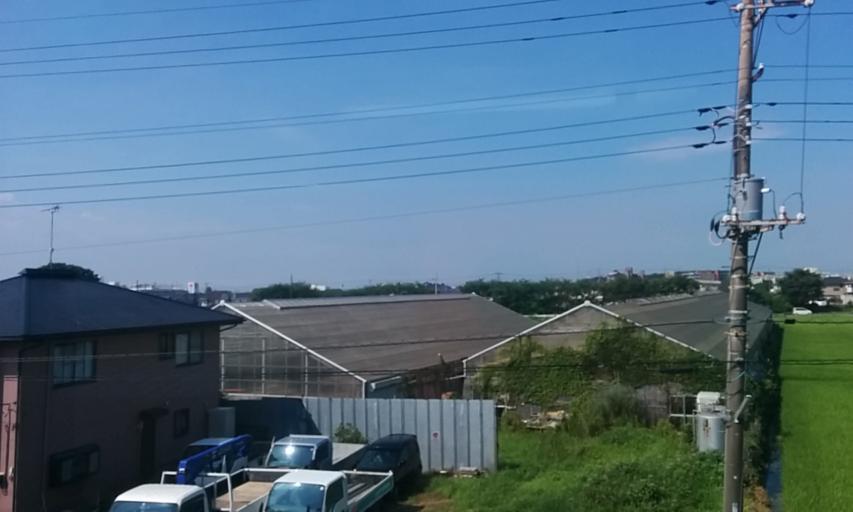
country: JP
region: Saitama
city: Kukichuo
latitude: 36.0804
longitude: 139.6778
